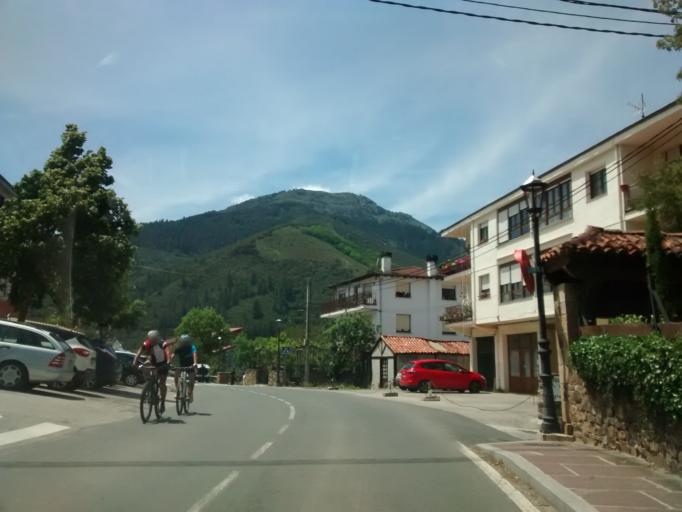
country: ES
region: Cantabria
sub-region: Provincia de Cantabria
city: Potes
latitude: 43.1527
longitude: -4.6224
